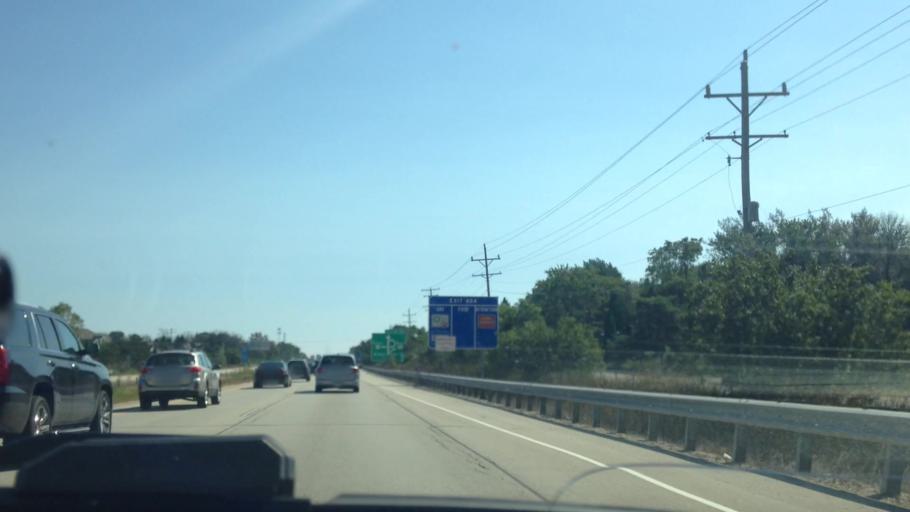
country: US
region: Wisconsin
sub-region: Milwaukee County
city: River Hills
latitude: 43.1873
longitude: -87.9228
